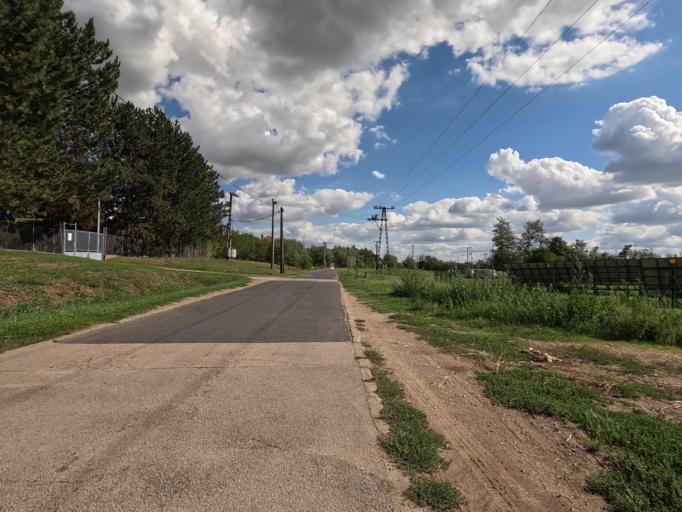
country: HU
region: Tolna
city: Dunaszentgyorgy
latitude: 46.5842
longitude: 18.8214
